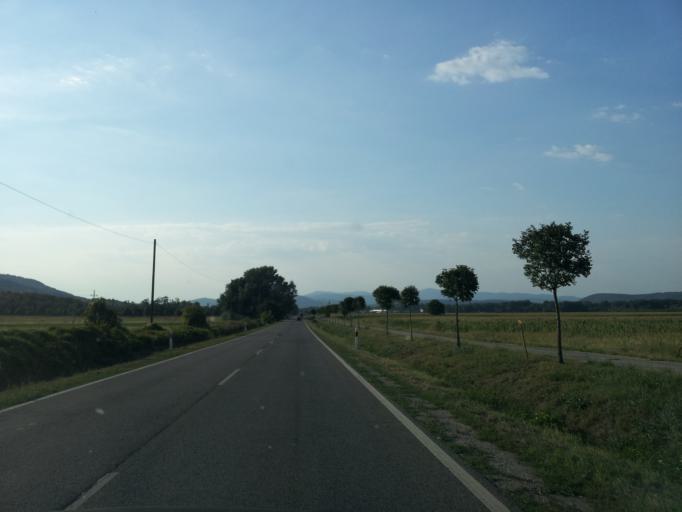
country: HU
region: Pest
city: Dunabogdany
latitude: 47.7761
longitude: 19.0551
